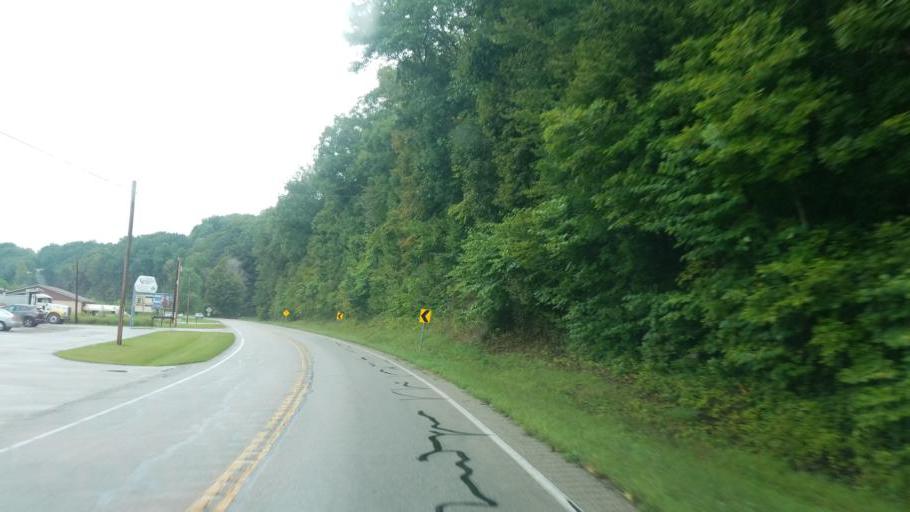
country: US
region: Kentucky
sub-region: Rowan County
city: Morehead
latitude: 38.1539
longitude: -83.4956
